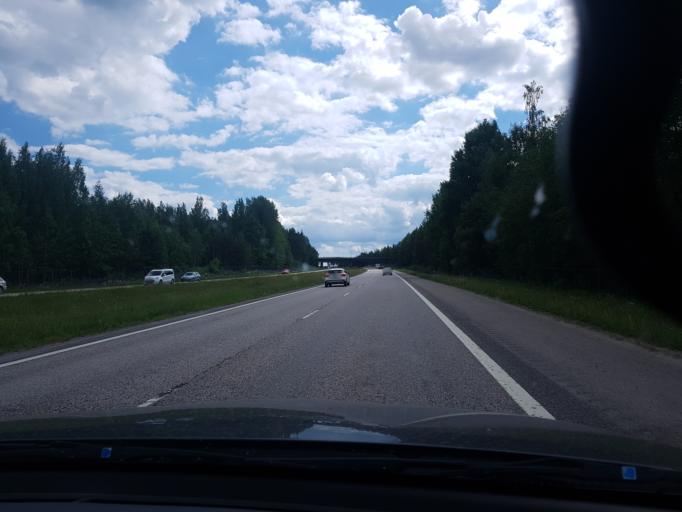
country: FI
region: Uusimaa
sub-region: Helsinki
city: Hyvinge
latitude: 60.5935
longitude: 24.7973
